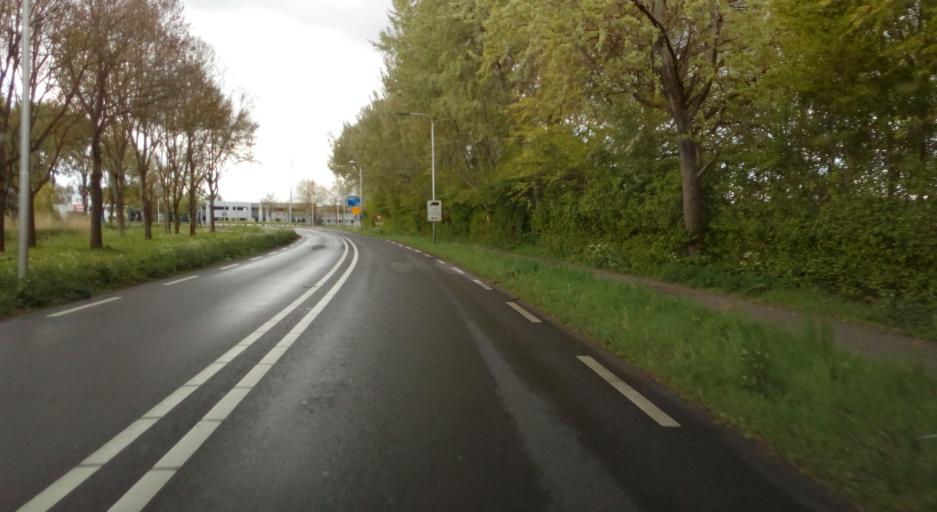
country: NL
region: South Holland
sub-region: Gemeente Zwijndrecht
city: Heerjansdam
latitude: 51.8153
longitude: 4.5942
